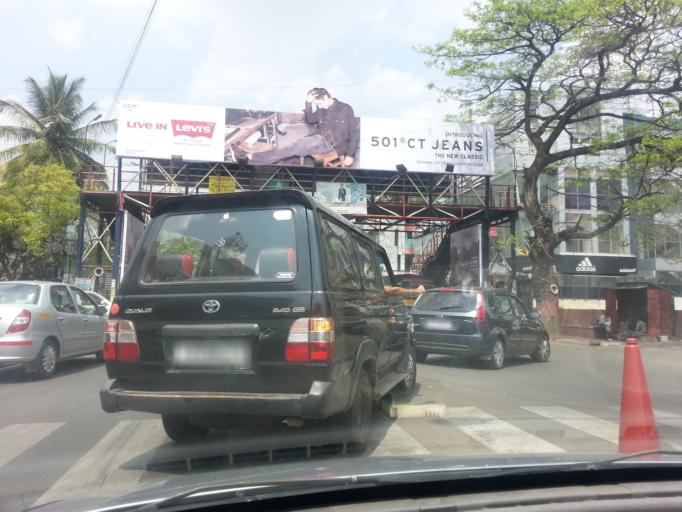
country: IN
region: Karnataka
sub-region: Bangalore Urban
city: Bangalore
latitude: 12.9633
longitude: 77.6416
